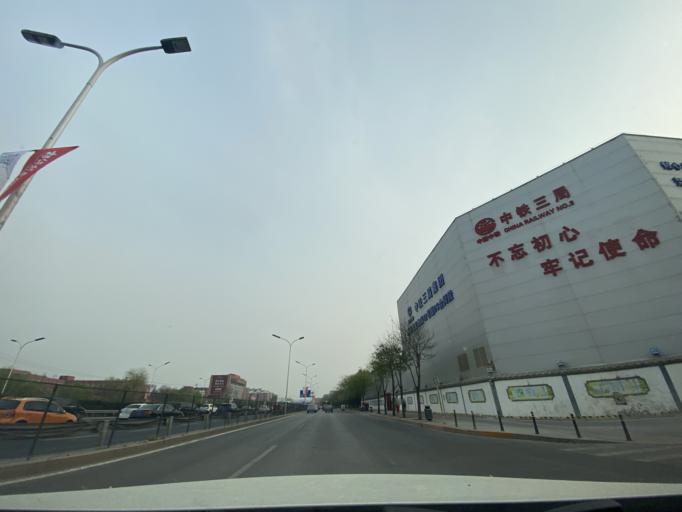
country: CN
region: Beijing
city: Sijiqing
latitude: 39.9399
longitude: 116.2678
